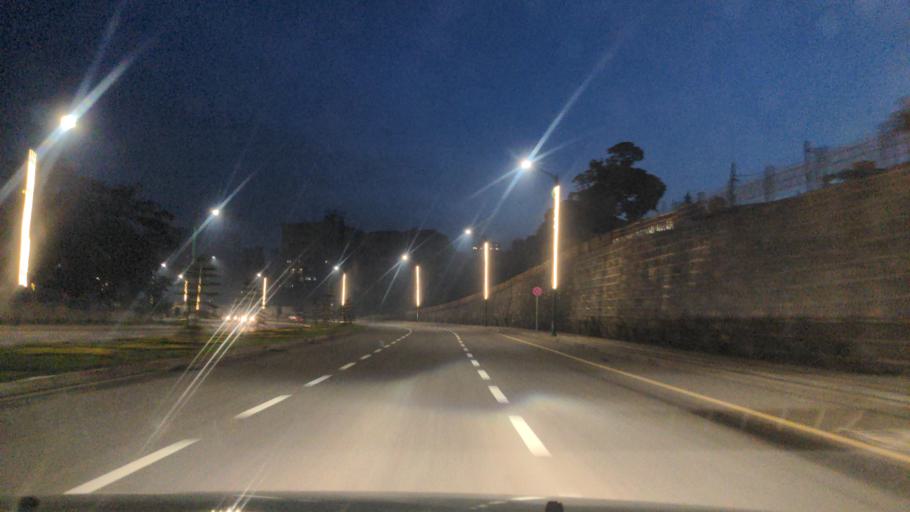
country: ET
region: Adis Abeba
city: Addis Ababa
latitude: 9.0059
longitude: 38.7744
